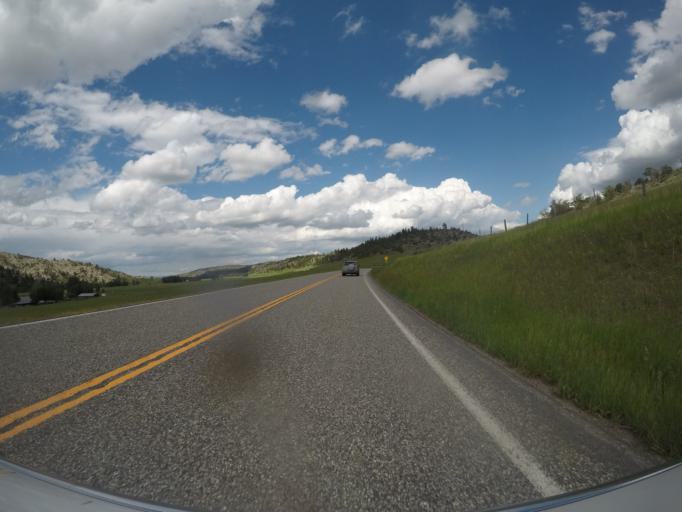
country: US
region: Montana
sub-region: Sweet Grass County
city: Big Timber
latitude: 45.7087
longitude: -110.0094
